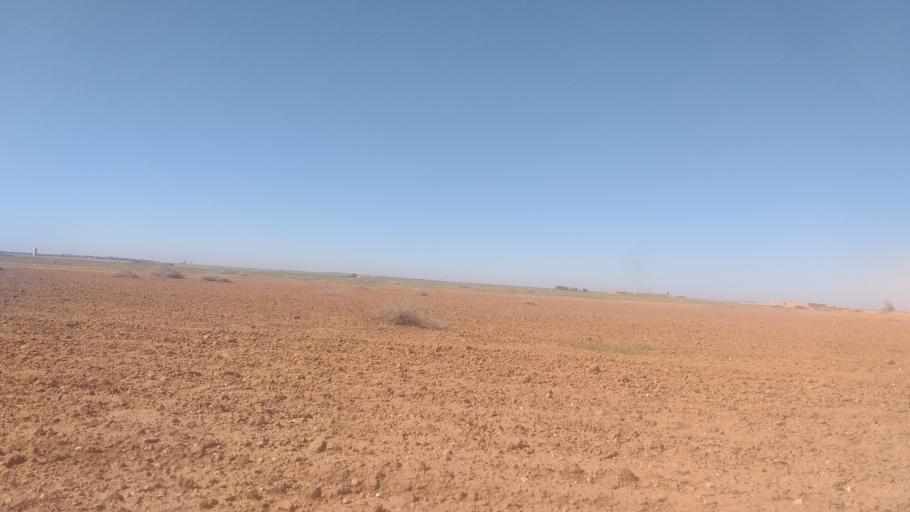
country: MA
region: Marrakech-Tensift-Al Haouz
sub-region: Kelaa-Des-Sraghna
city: Sidi Bou Othmane
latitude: 32.1478
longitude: -7.8596
